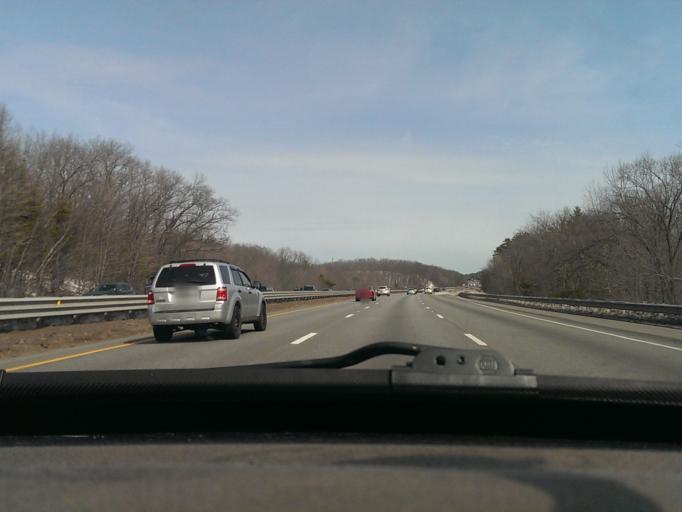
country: US
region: Massachusetts
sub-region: Worcester County
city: Charlton
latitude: 42.1729
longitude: -71.9262
